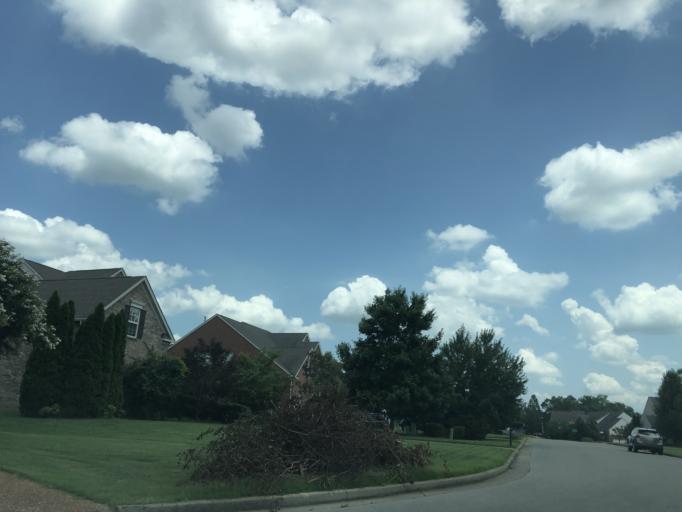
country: US
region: Tennessee
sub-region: Williamson County
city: Brentwood Estates
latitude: 36.0092
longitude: -86.7280
